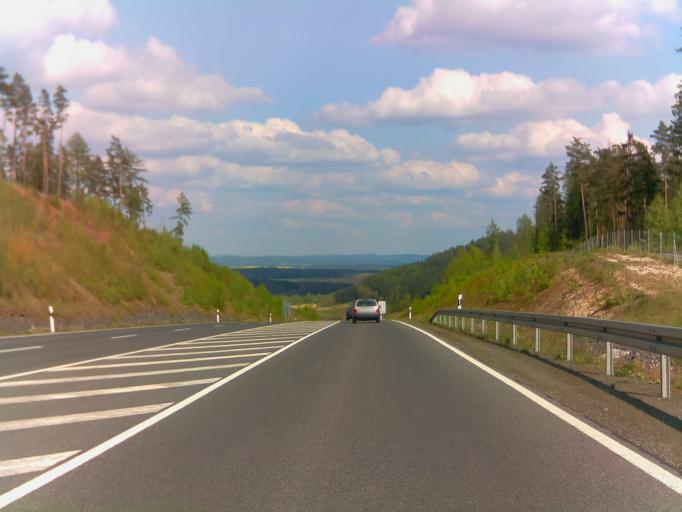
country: DE
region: Bavaria
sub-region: Upper Franconia
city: Rodental
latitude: 50.3053
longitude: 11.0489
